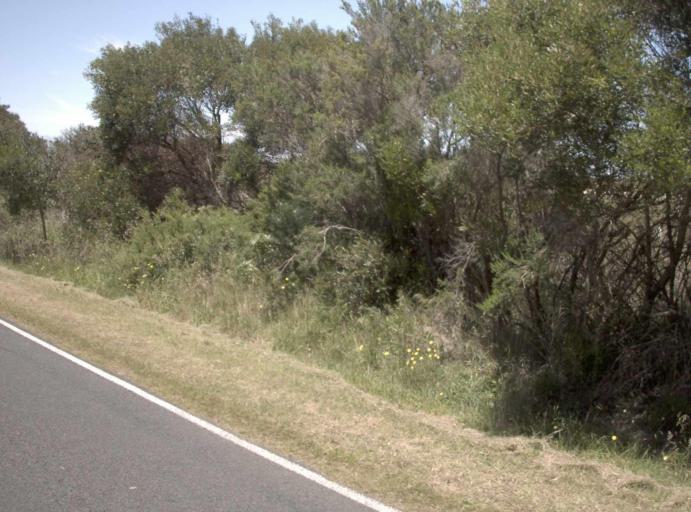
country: AU
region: Victoria
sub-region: Latrobe
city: Morwell
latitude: -38.7860
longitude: 146.1697
